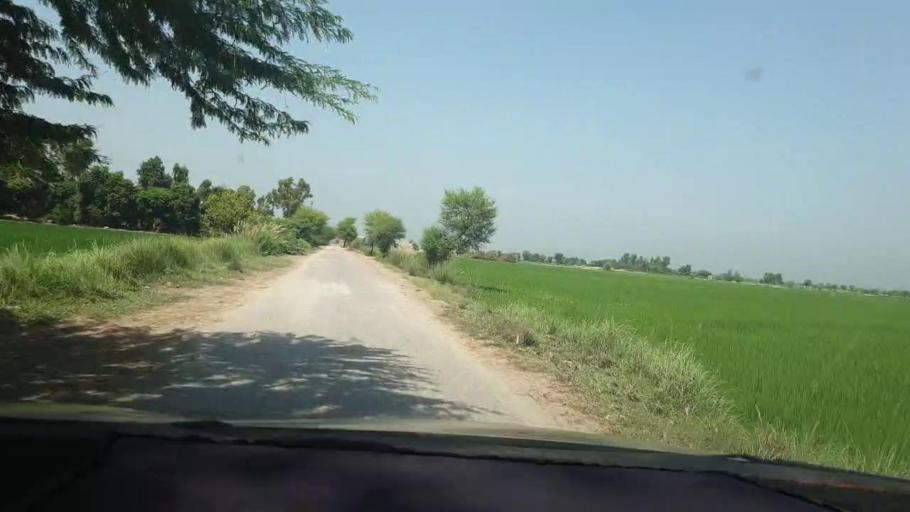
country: PK
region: Sindh
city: Kambar
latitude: 27.6117
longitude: 68.0594
